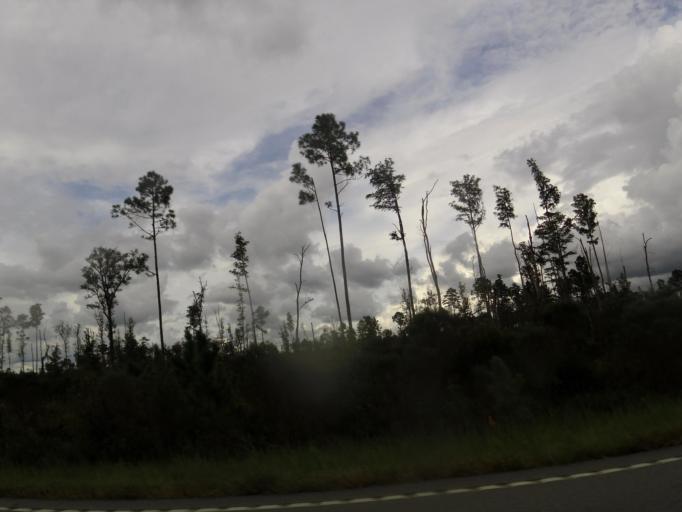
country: US
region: Florida
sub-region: Baker County
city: Macclenny
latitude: 30.5242
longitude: -82.1639
